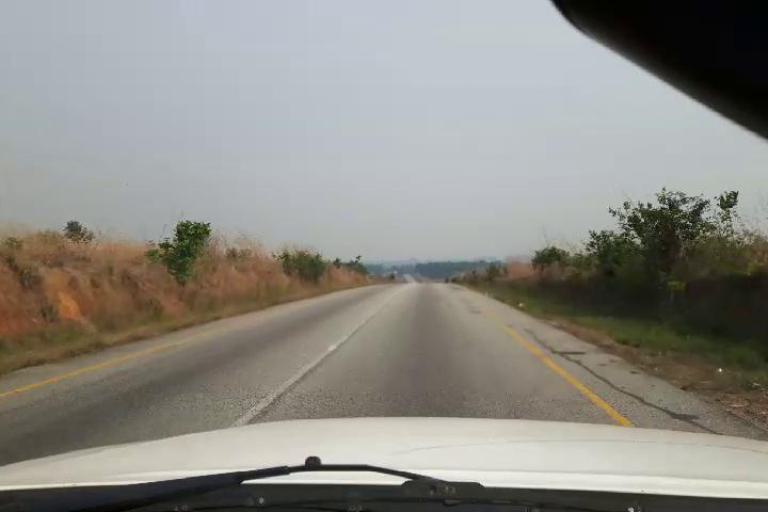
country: SL
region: Southern Province
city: Largo
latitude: 8.2273
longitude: -12.0774
